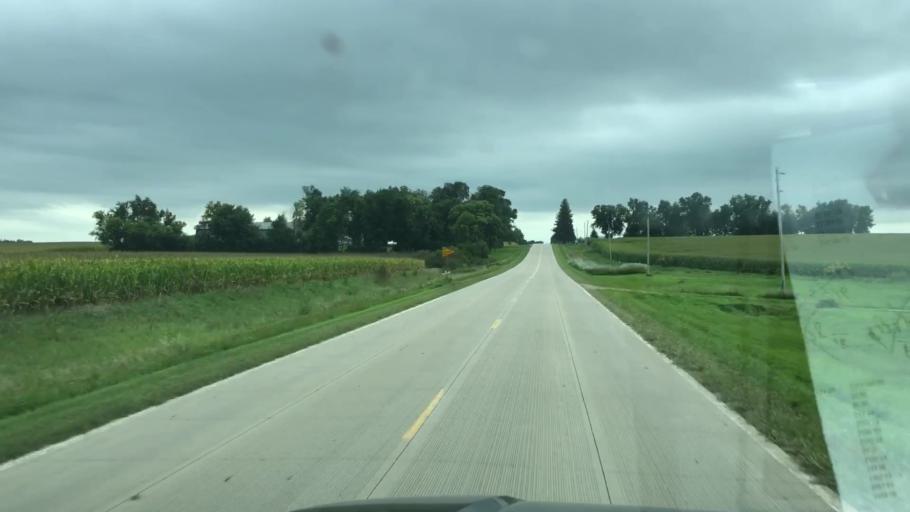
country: US
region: Iowa
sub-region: Sioux County
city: Alton
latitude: 43.1123
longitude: -95.9787
